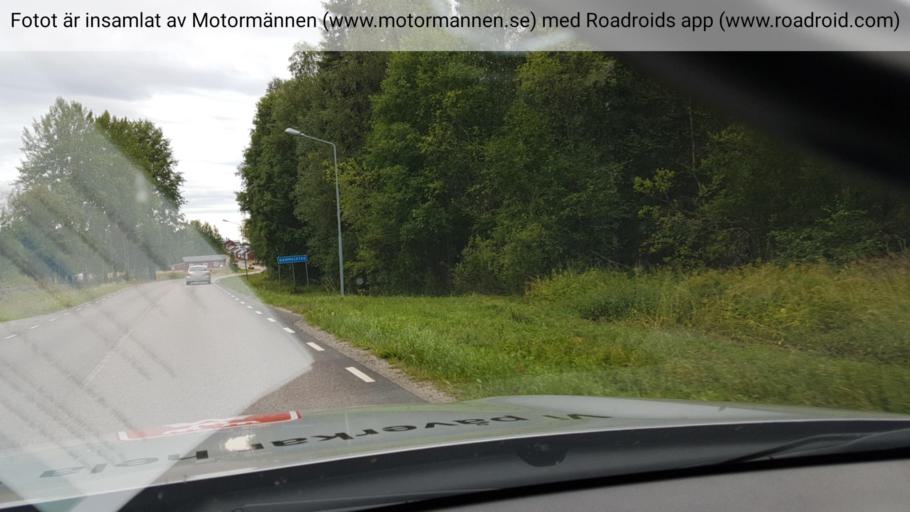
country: SE
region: Norrbotten
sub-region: Lulea Kommun
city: Gammelstad
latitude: 65.6502
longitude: 22.0311
